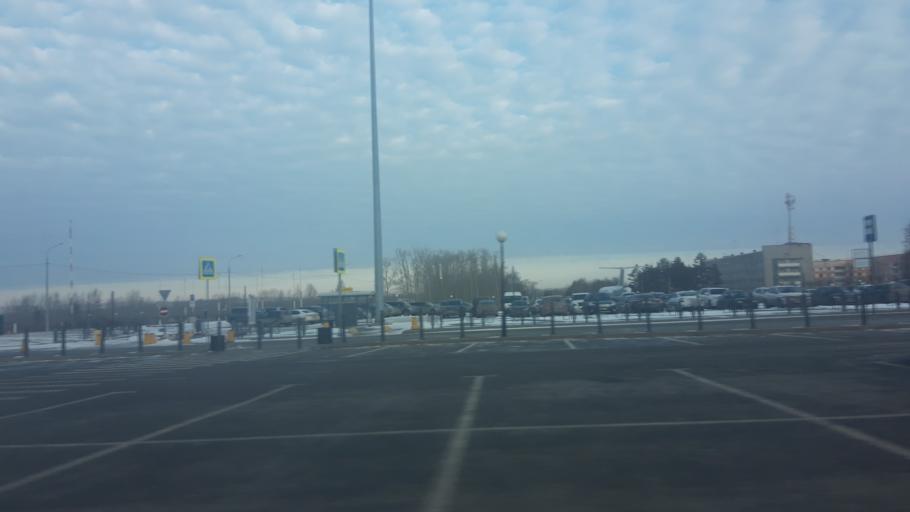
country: RU
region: Tjumen
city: Moskovskiy
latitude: 57.1820
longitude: 65.3491
